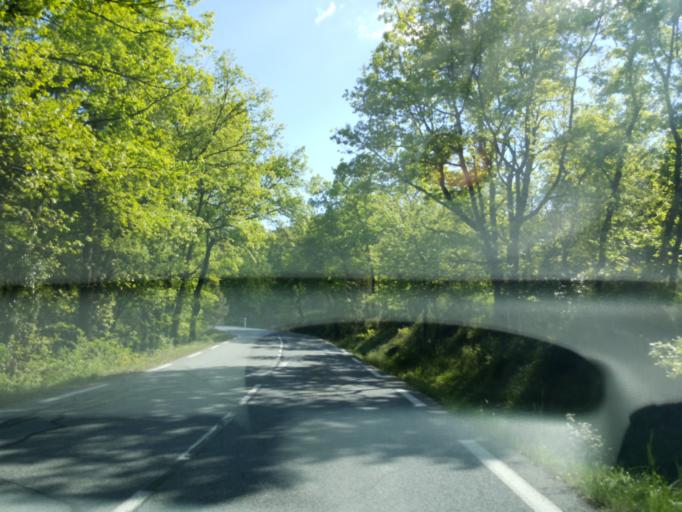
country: FR
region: Provence-Alpes-Cote d'Azur
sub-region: Departement du Var
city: La Roquebrussanne
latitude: 43.3701
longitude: 5.9721
